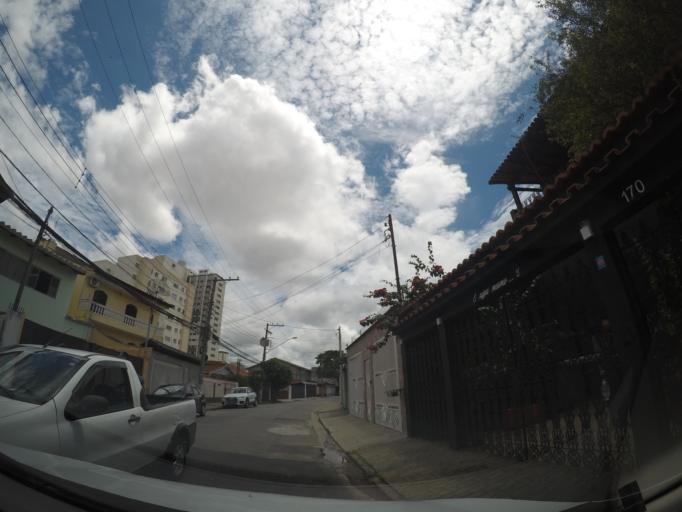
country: BR
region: Sao Paulo
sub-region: Guarulhos
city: Guarulhos
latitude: -23.4640
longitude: -46.5246
